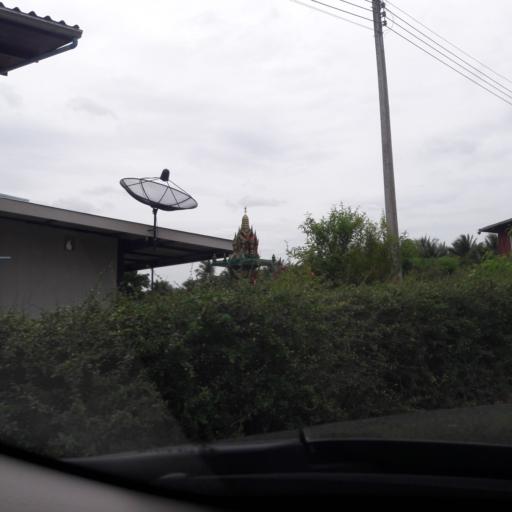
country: TH
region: Ratchaburi
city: Damnoen Saduak
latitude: 13.5768
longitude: 99.9366
